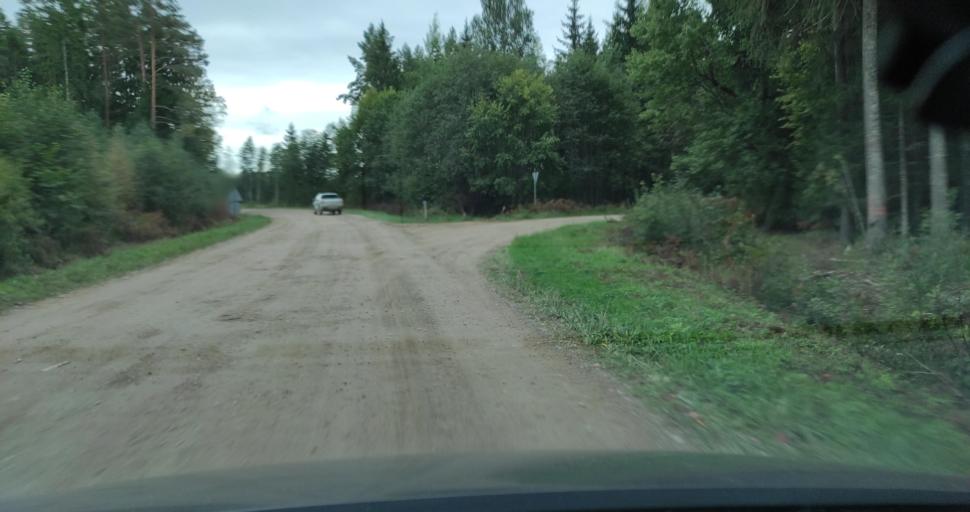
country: LV
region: Talsu Rajons
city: Stende
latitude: 57.0406
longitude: 22.3088
